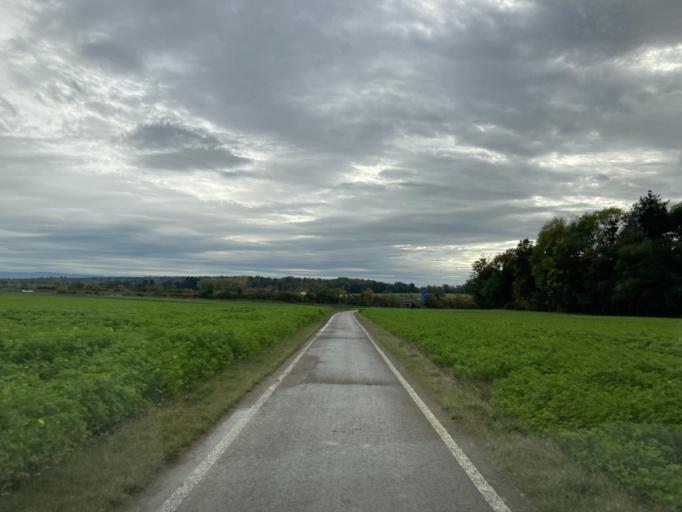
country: DE
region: Baden-Wuerttemberg
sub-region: Regierungsbezirk Stuttgart
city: Bondorf
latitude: 48.5133
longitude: 8.8546
